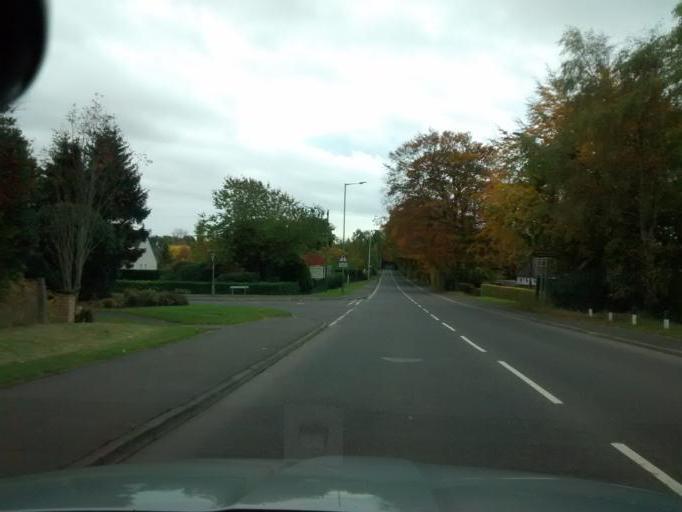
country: GB
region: Scotland
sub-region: Perth and Kinross
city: Blairgowrie
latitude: 56.5759
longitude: -3.3473
